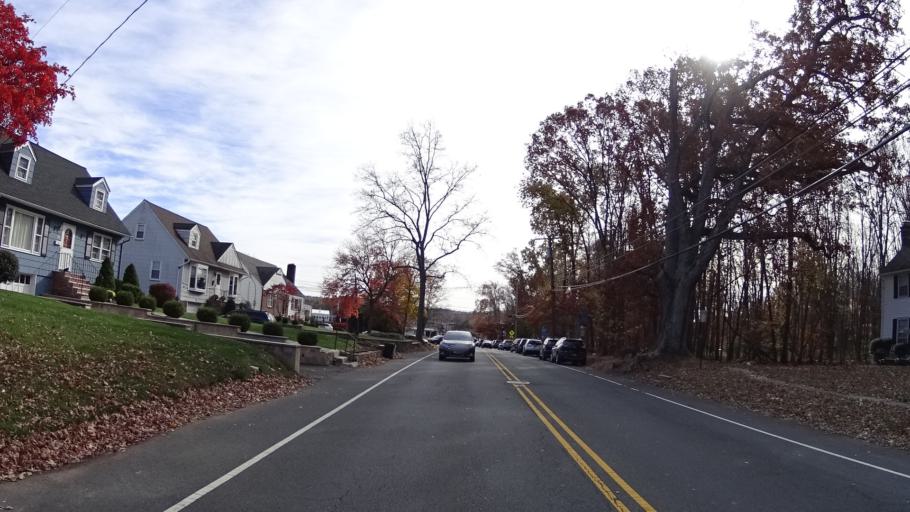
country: US
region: New Jersey
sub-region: Union County
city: New Providence
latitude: 40.7083
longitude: -74.4068
